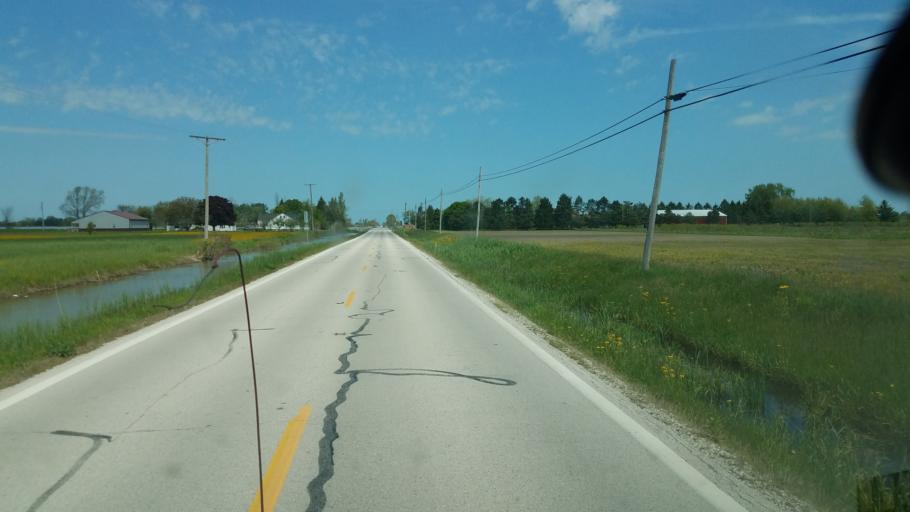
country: US
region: Ohio
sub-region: Ottawa County
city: Oak Harbor
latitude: 41.5719
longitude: -83.1449
